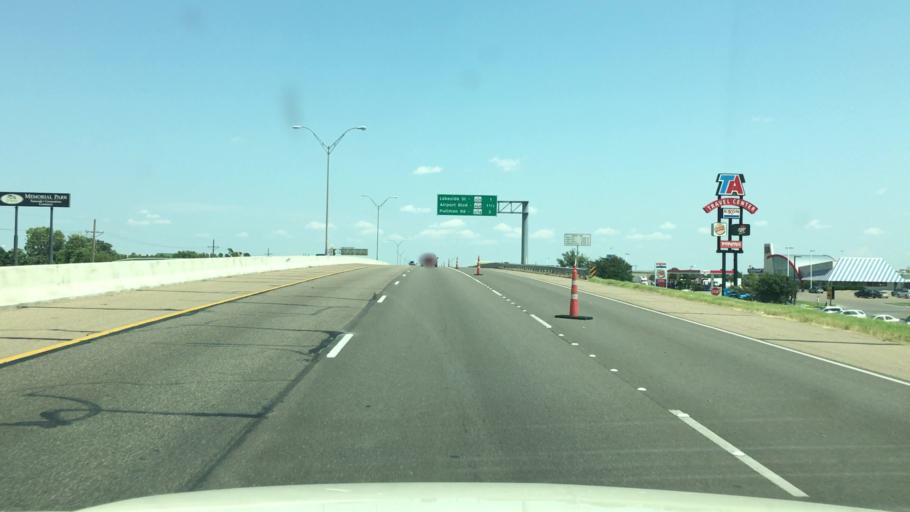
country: US
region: Texas
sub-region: Potter County
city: Amarillo
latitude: 35.1926
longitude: -101.7615
